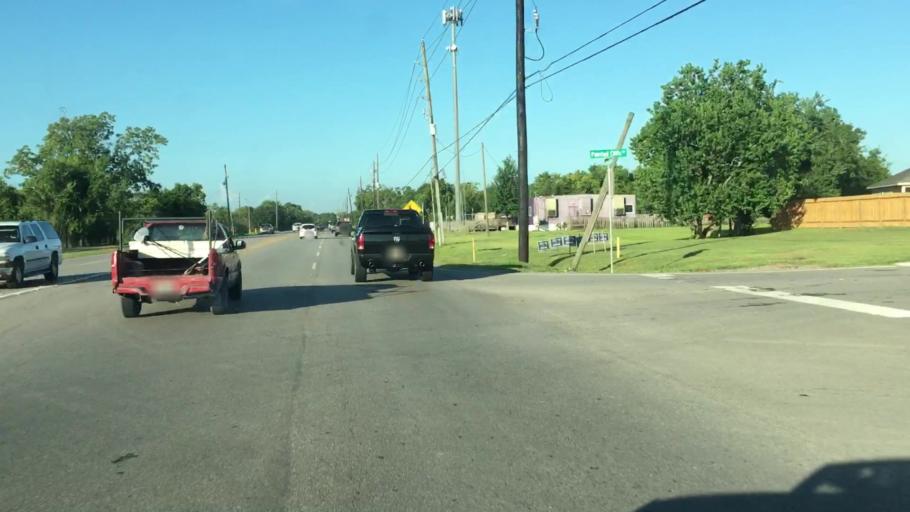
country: US
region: Texas
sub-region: Harris County
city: Humble
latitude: 29.9682
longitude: -95.2363
